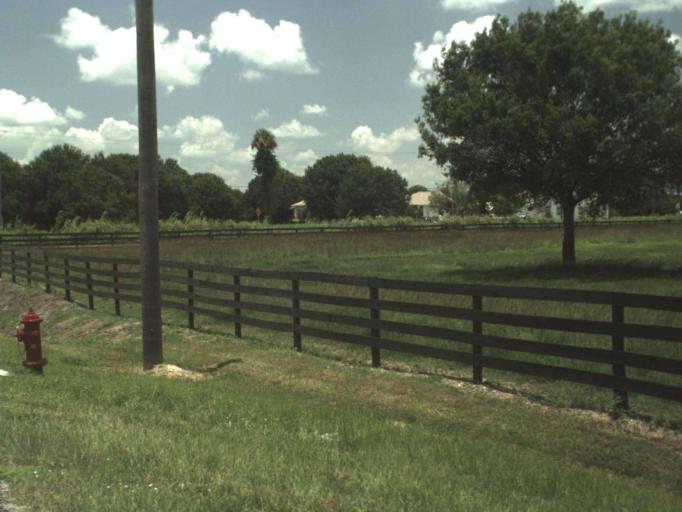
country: US
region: Florida
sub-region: Saint Lucie County
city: Fort Pierce South
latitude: 27.3744
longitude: -80.4394
